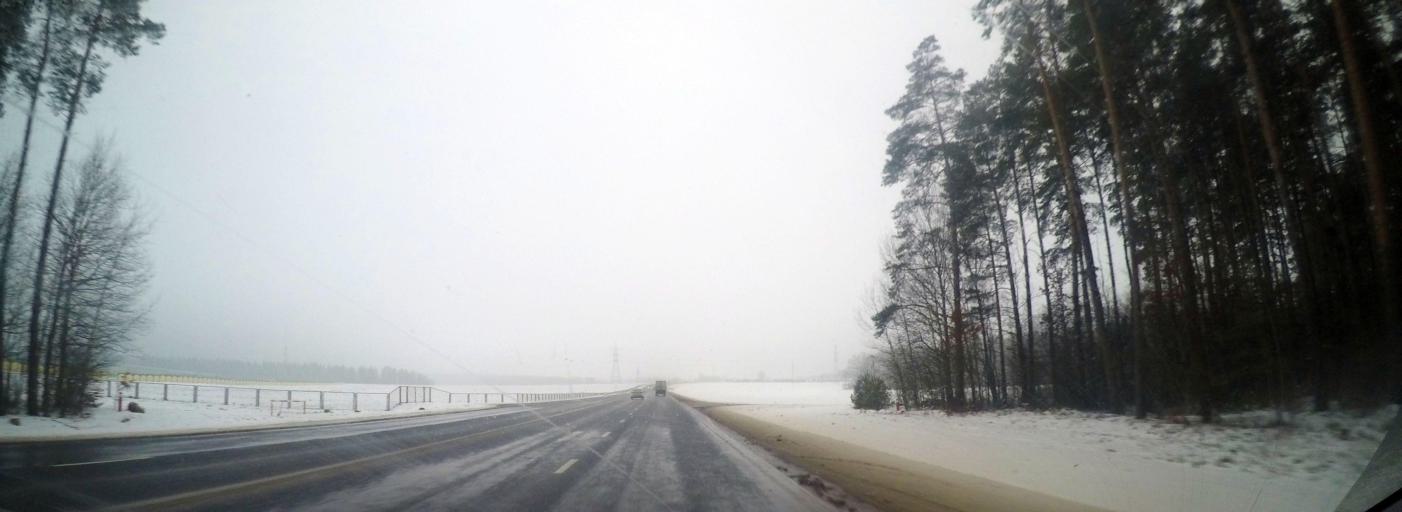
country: BY
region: Grodnenskaya
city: Hrodna
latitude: 53.6246
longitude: 23.8786
